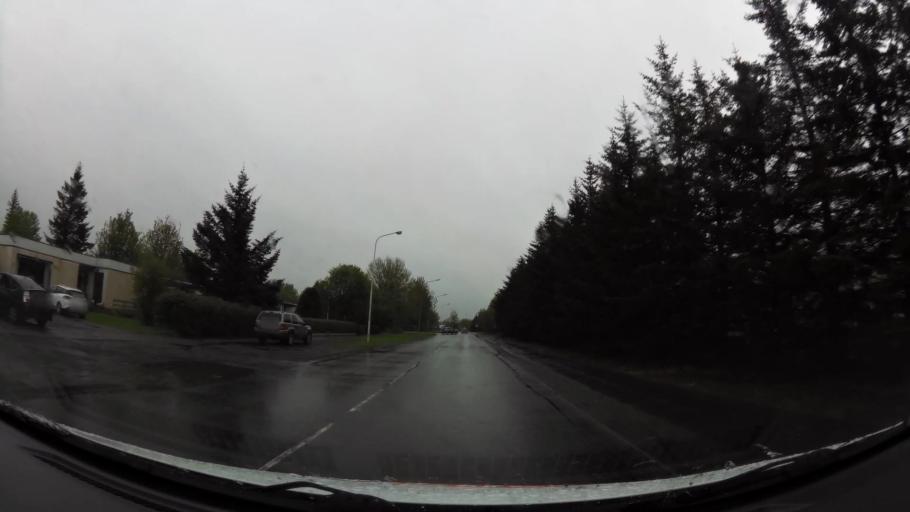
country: IS
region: South
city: Selfoss
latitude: 63.9334
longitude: -21.0095
